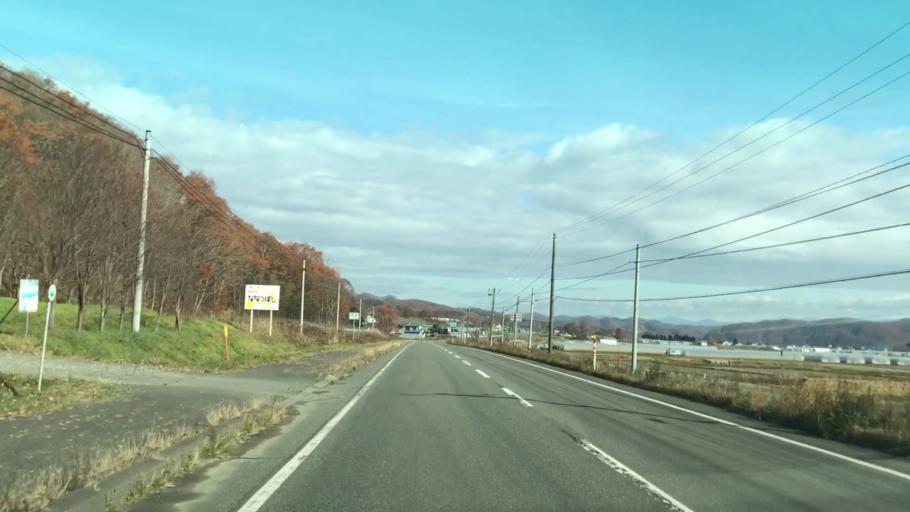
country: JP
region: Hokkaido
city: Shizunai-furukawacho
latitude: 42.5680
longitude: 142.0951
